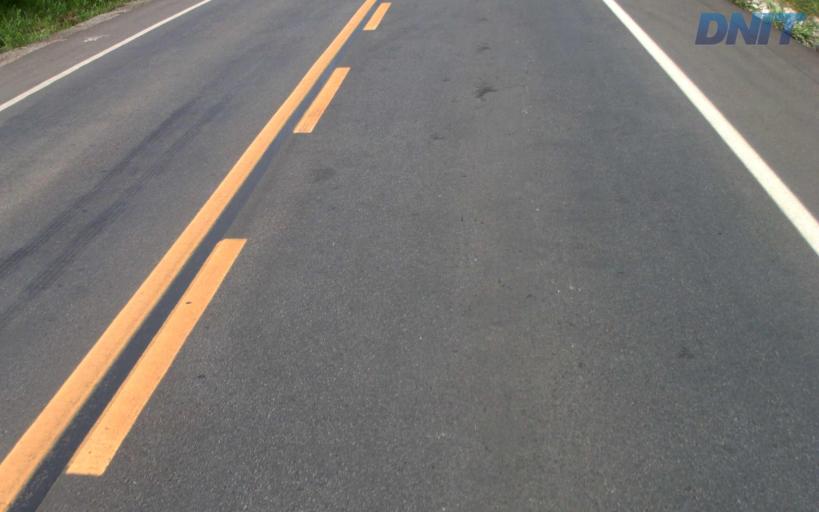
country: BR
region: Minas Gerais
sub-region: Belo Oriente
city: Belo Oriente
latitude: -19.2411
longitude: -42.3346
